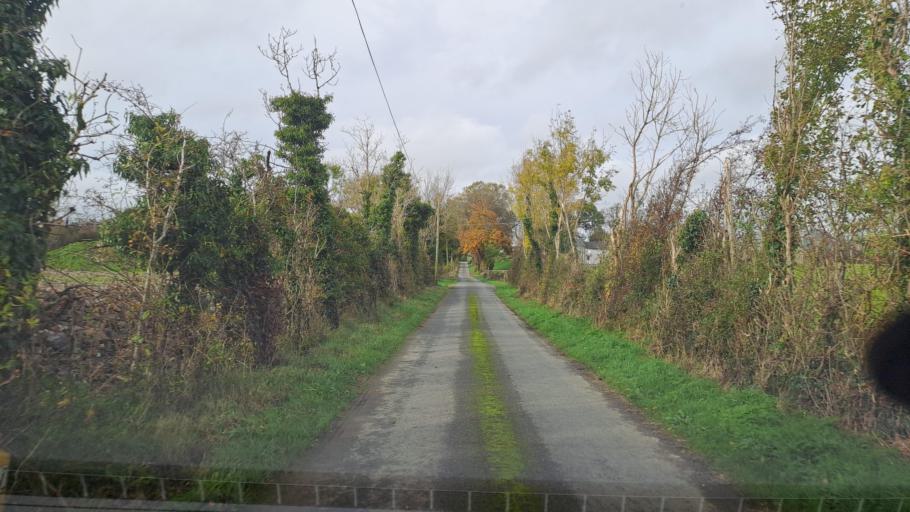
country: IE
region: Ulster
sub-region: An Cabhan
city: Kingscourt
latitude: 54.0329
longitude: -6.8488
